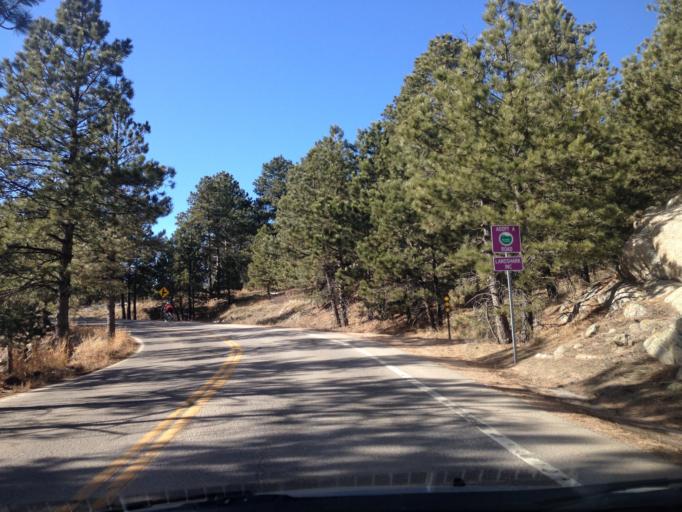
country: US
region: Colorado
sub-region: Boulder County
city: Boulder
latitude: 39.9978
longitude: -105.3077
